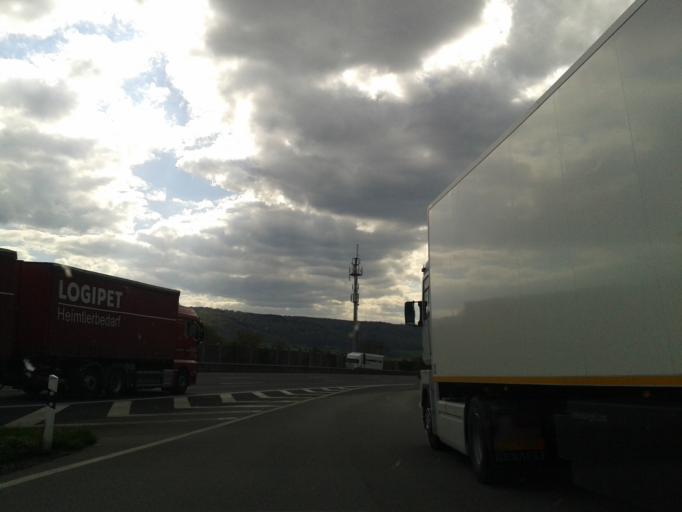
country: DE
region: Lower Saxony
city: Scheden
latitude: 51.3955
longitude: 9.7791
